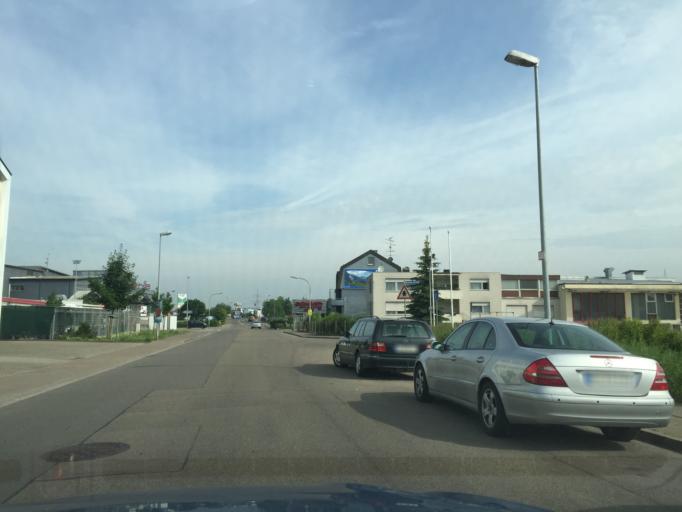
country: DE
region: Bavaria
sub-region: Swabia
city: Senden
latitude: 48.3289
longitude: 10.0429
